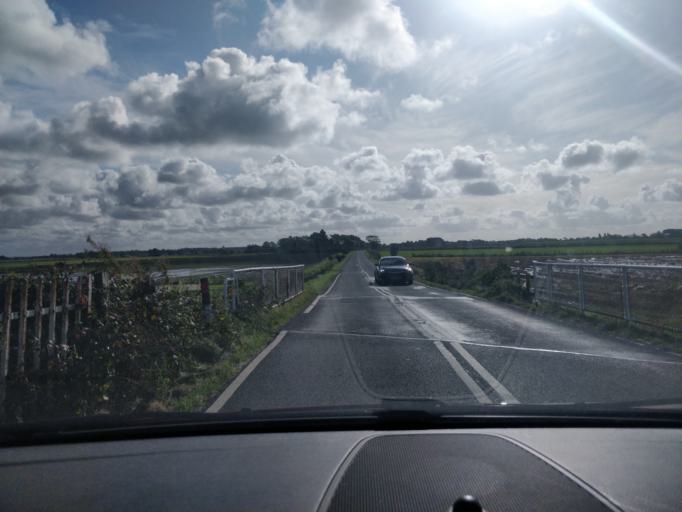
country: GB
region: England
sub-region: Lancashire
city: Banks
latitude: 53.6311
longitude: -2.9425
